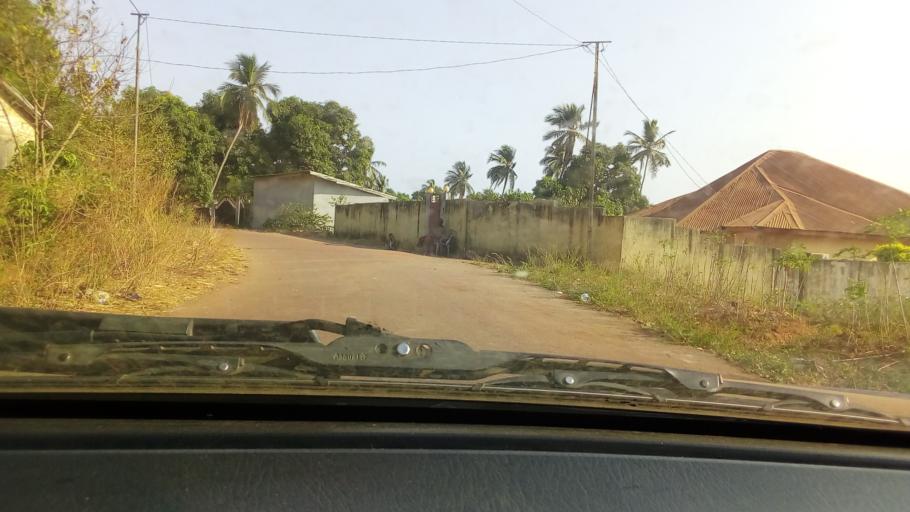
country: GN
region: Kindia
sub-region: Prefecture de Dubreka
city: Dubreka
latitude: 9.7884
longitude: -13.5274
